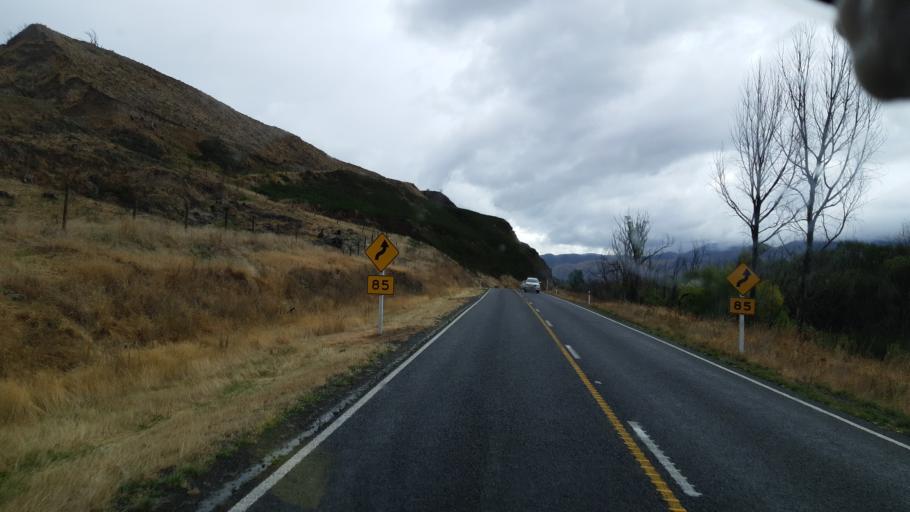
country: NZ
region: Canterbury
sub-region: Hurunui District
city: Amberley
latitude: -42.5783
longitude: 172.7454
